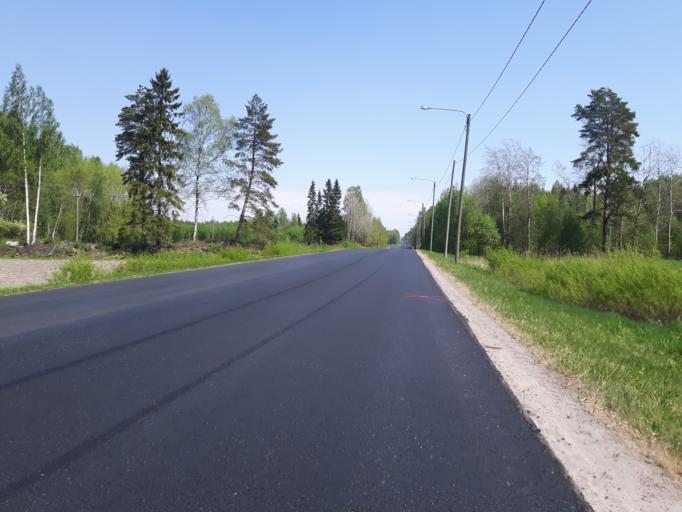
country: FI
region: Uusimaa
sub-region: Helsinki
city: Nickby
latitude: 60.3184
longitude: 25.4082
